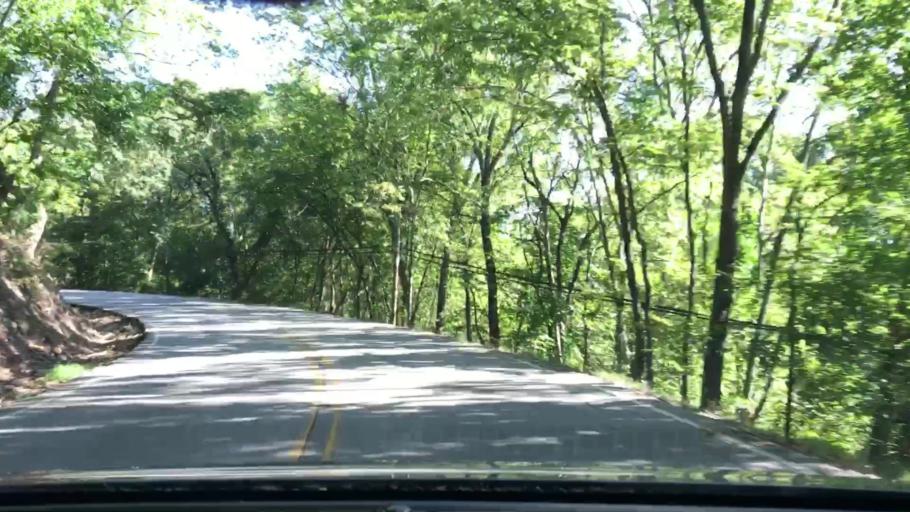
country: US
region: Tennessee
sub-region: Smith County
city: Carthage
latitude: 36.3063
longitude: -85.9508
